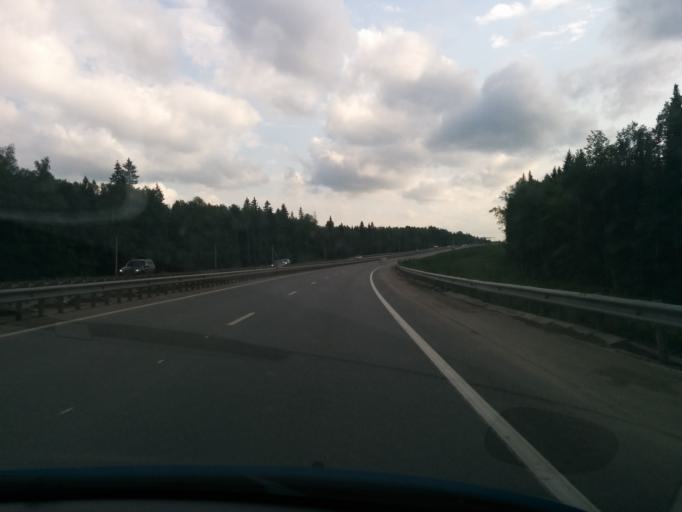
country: RU
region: Perm
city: Novyye Lyady
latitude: 58.0315
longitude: 56.4332
